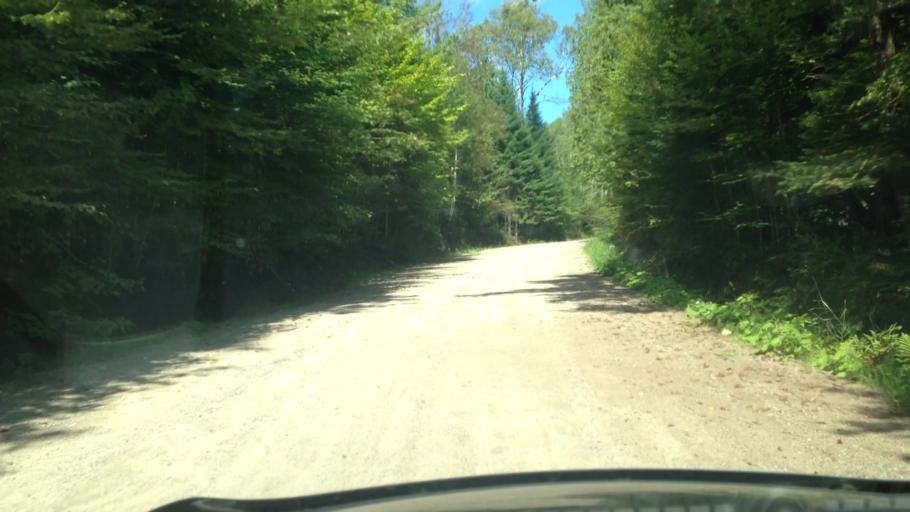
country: CA
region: Quebec
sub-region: Laurentides
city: Brownsburg-Chatham
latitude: 45.9208
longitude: -74.5800
